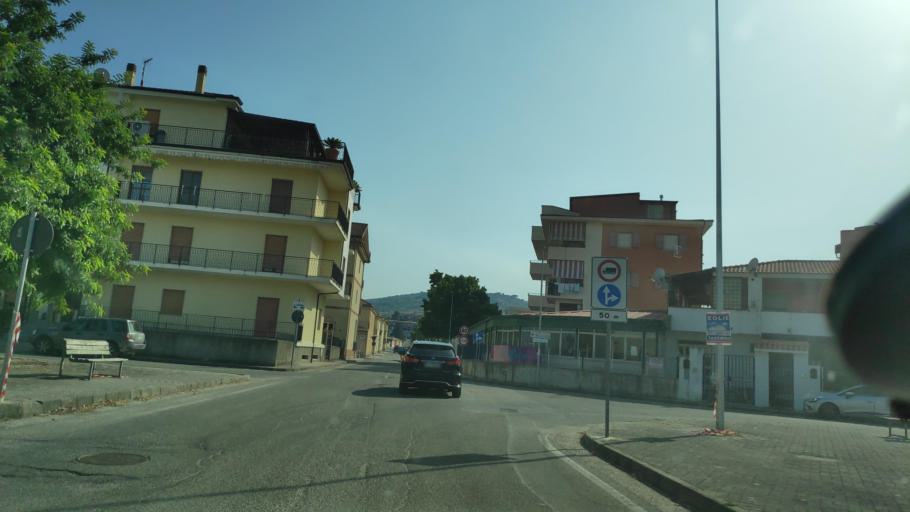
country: IT
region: Calabria
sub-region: Provincia di Catanzaro
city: Isca Marina
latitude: 38.6053
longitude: 16.5557
